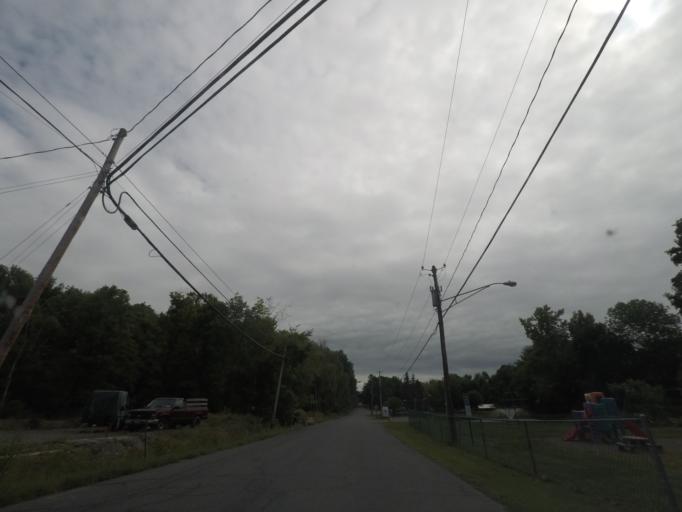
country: US
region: New York
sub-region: Rensselaer County
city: Nassau
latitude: 42.5134
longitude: -73.6093
